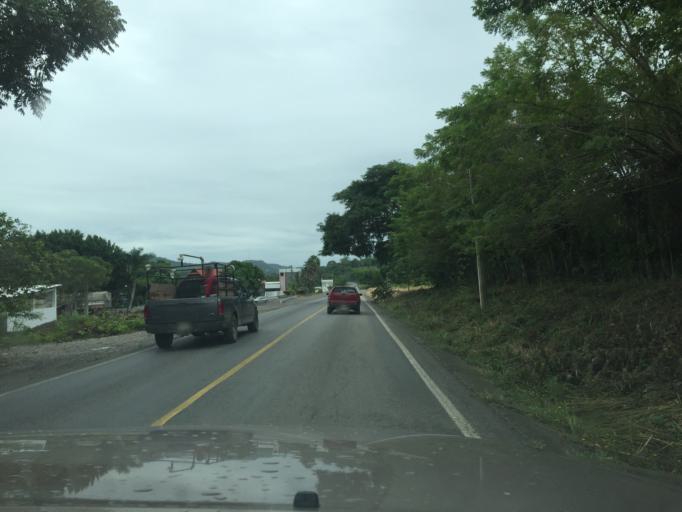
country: MX
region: Veracruz
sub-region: Papantla
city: El Chote
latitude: 20.4393
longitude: -97.3970
